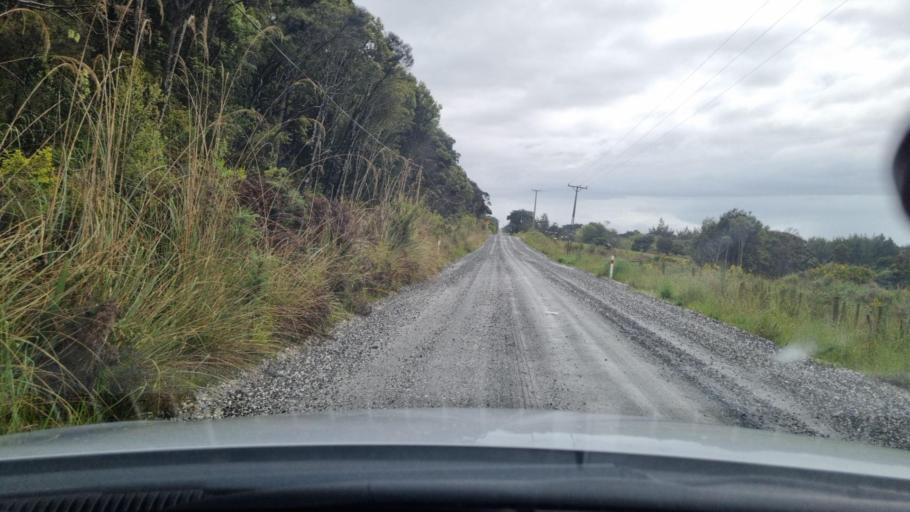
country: NZ
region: Southland
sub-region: Invercargill City
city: Bluff
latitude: -46.5375
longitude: 168.2652
